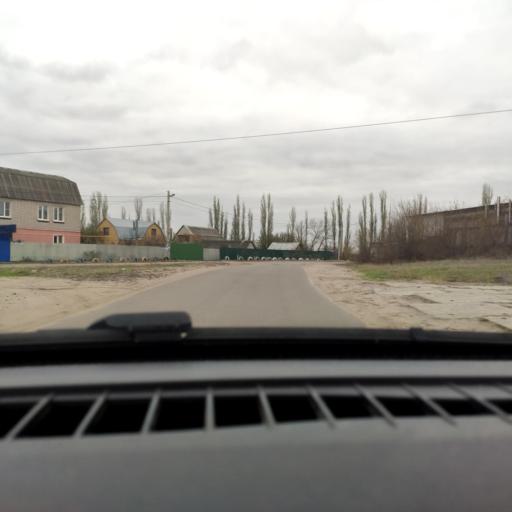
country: RU
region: Voronezj
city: Maslovka
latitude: 51.5778
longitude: 39.3050
